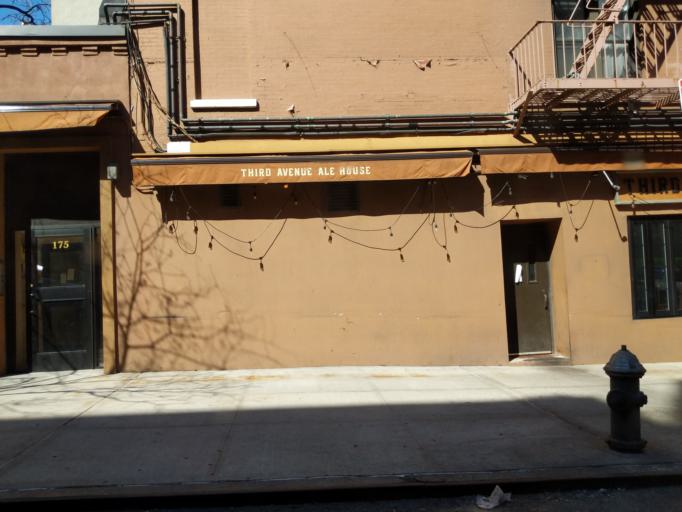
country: US
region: New York
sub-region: New York County
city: Manhattan
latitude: 40.7828
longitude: -73.9515
